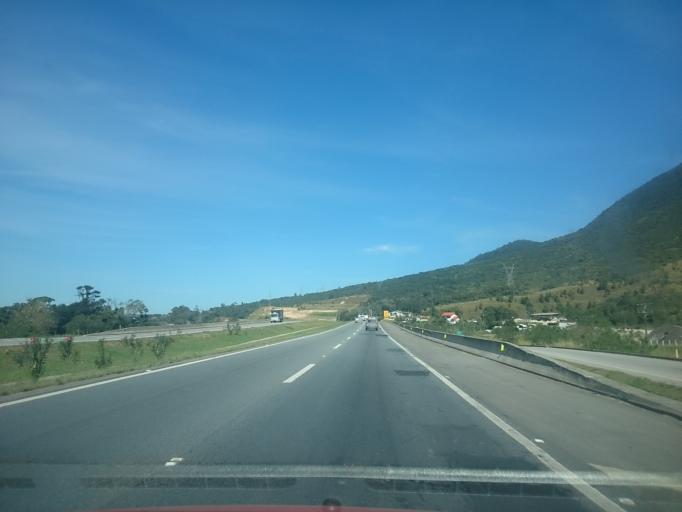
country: BR
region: Santa Catarina
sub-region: Palhoca
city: Palhoca
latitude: -27.7038
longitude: -48.6589
